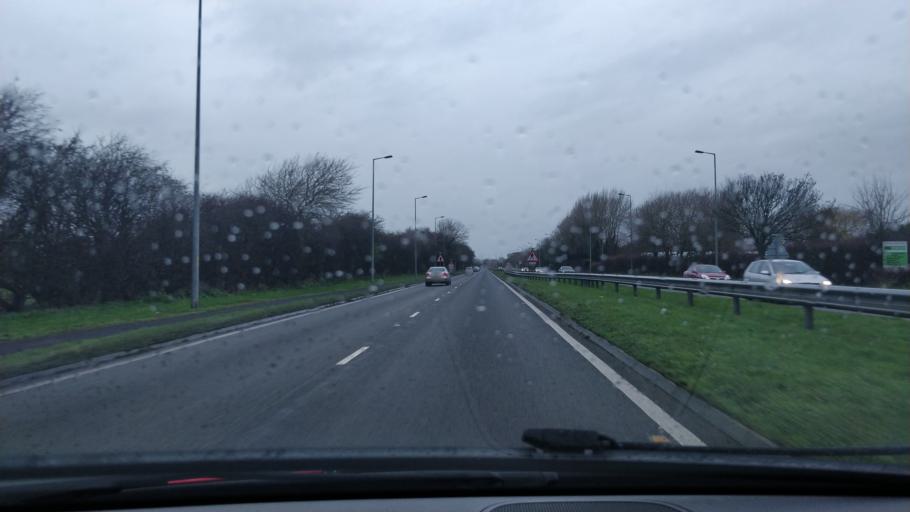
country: GB
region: England
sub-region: Sefton
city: Formby
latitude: 53.5607
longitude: -3.0463
